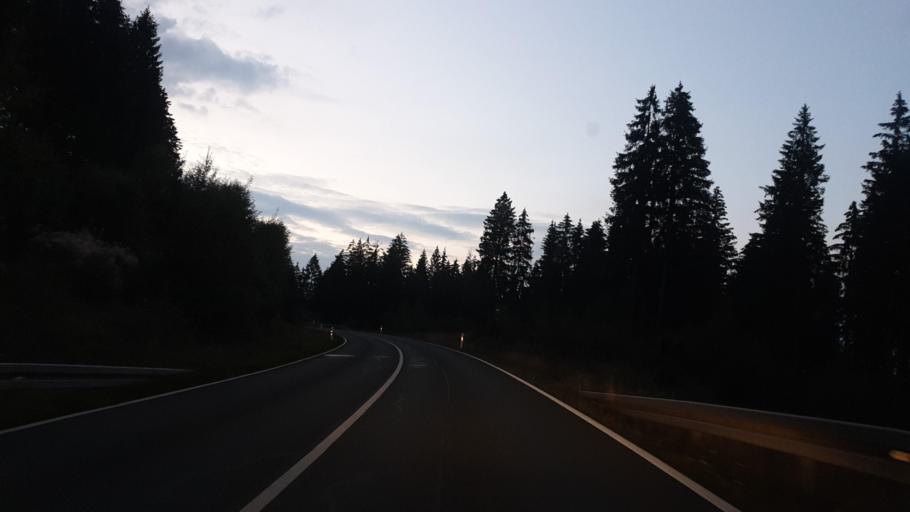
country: DE
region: Saxony
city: Schoenheide
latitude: 50.5077
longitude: 12.4851
